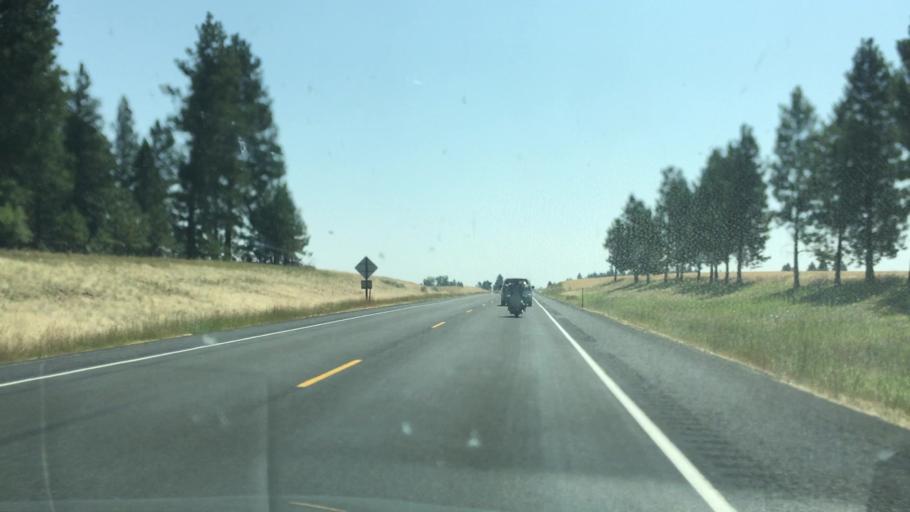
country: US
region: Idaho
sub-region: Nez Perce County
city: Lapwai
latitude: 46.2456
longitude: -116.5915
